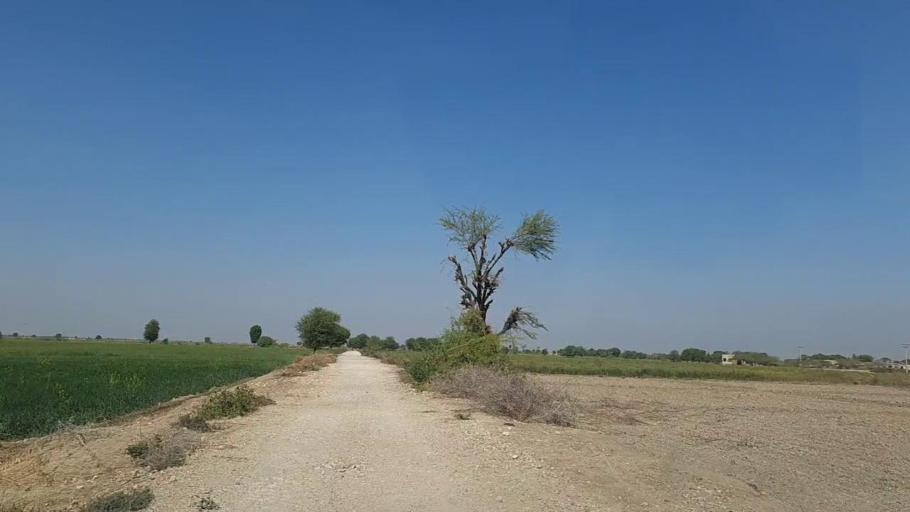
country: PK
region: Sindh
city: Pithoro
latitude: 25.4144
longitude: 69.4077
